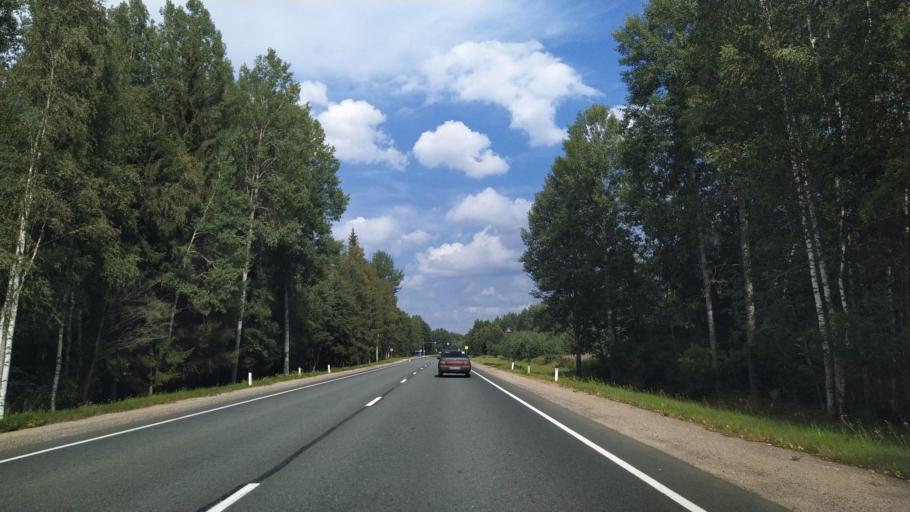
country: RU
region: Pskov
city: Porkhov
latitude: 57.8602
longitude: 29.5699
